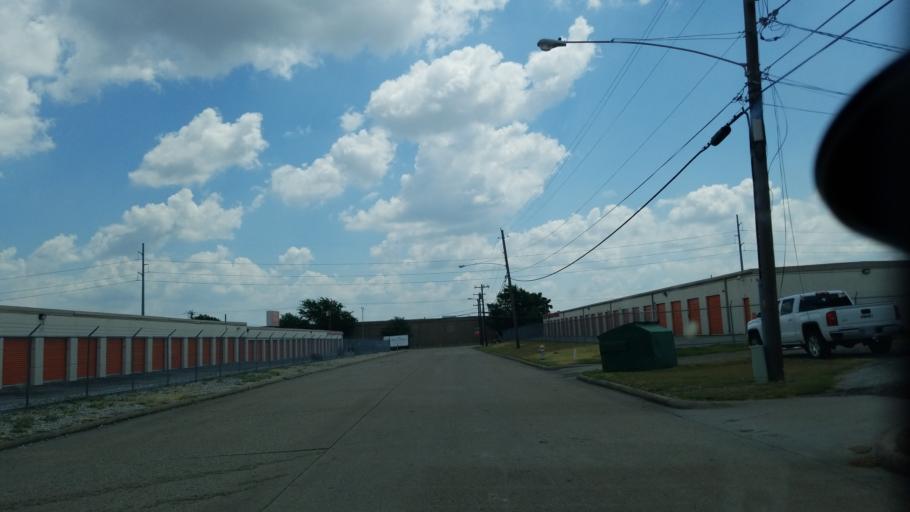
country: US
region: Texas
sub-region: Dallas County
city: Duncanville
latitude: 32.6844
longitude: -96.8931
